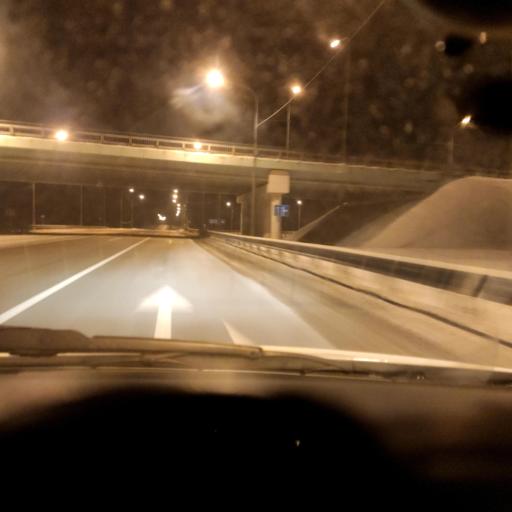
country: RU
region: Kursk
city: Fatezh
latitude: 52.0977
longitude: 35.8214
